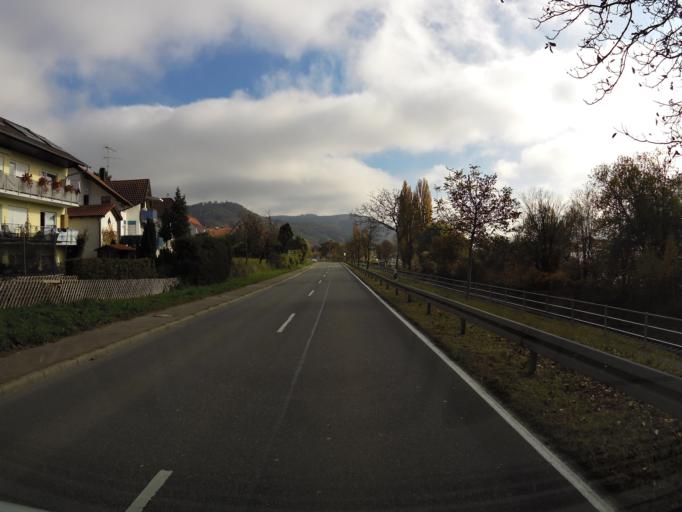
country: DE
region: Baden-Wuerttemberg
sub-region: Freiburg Region
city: Bodman-Ludwigshafen
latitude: 47.8170
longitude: 9.0468
